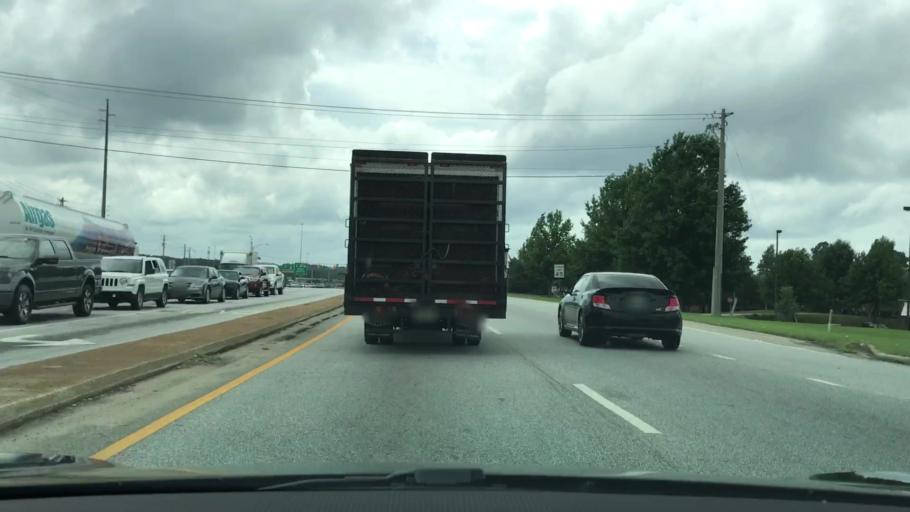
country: US
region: Alabama
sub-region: Lee County
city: Opelika
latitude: 32.6225
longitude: -85.4050
